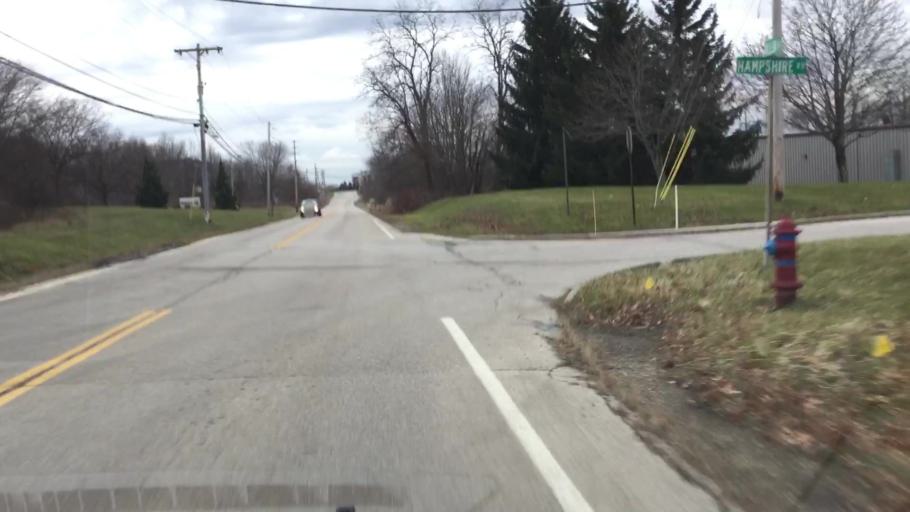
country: US
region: Ohio
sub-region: Summit County
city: Silver Lake
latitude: 41.1886
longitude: -81.4735
